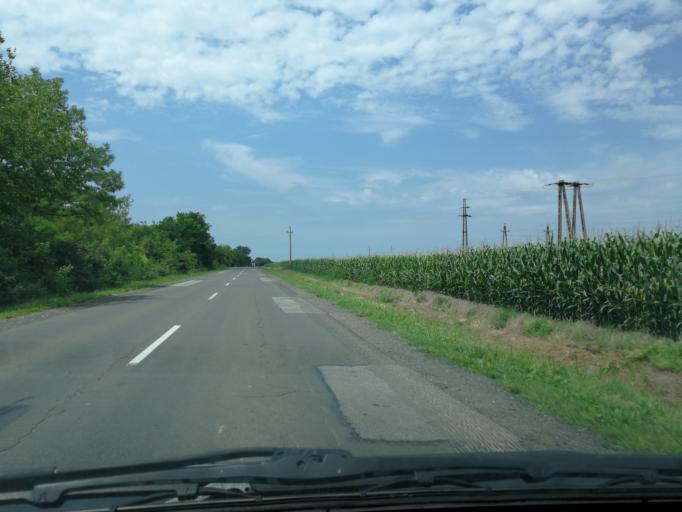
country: HU
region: Baranya
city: Siklos
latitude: 45.8497
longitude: 18.3501
